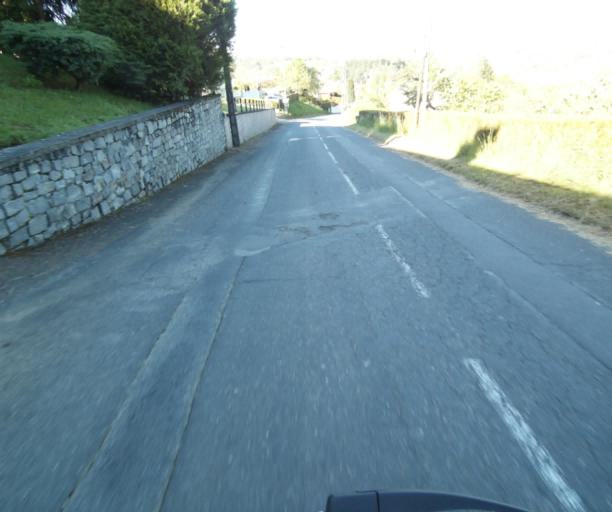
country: FR
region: Limousin
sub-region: Departement de la Correze
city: Tulle
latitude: 45.2662
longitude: 1.7842
